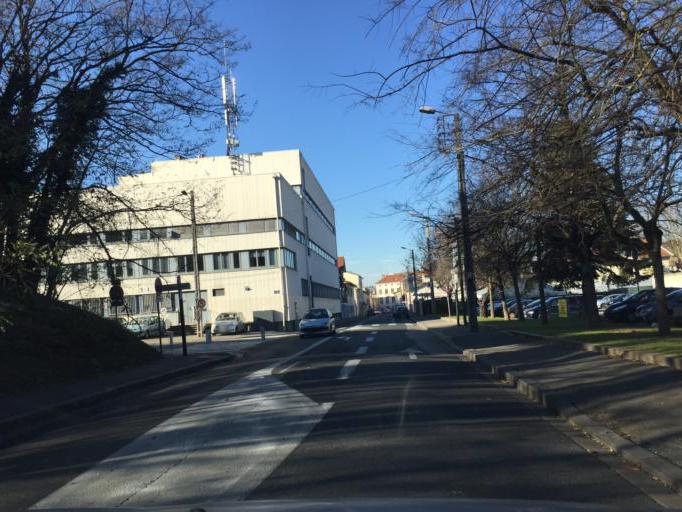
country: FR
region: Rhone-Alpes
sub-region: Departement du Rhone
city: Caluire-et-Cuire
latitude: 45.7986
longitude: 4.8498
